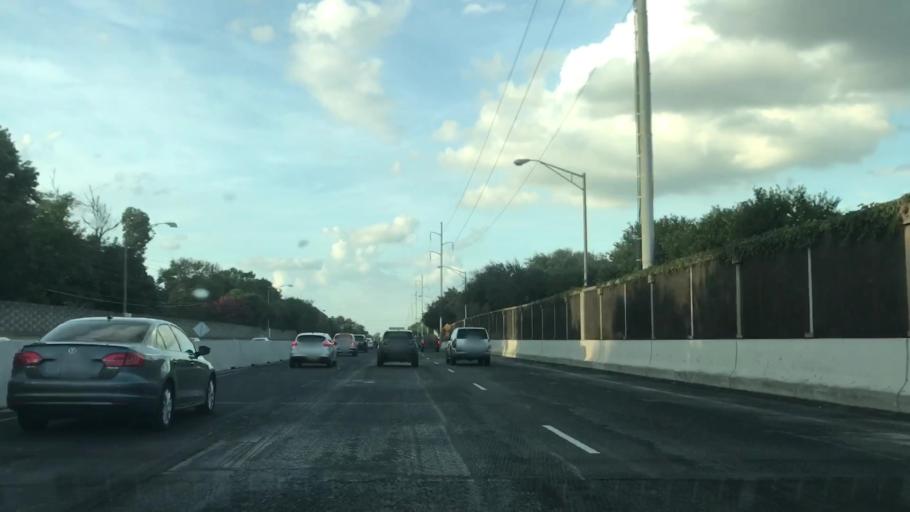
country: US
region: Texas
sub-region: Dallas County
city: University Park
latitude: 32.8425
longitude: -96.8142
